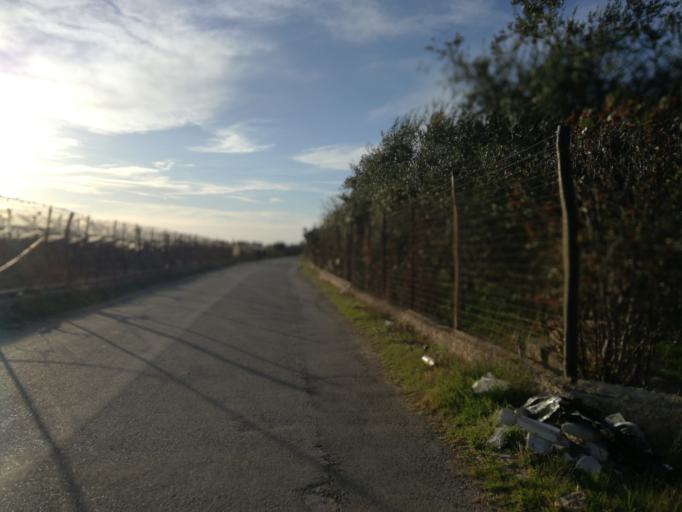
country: IT
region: Apulia
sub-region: Provincia di Bari
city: Capurso
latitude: 41.0503
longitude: 16.9032
